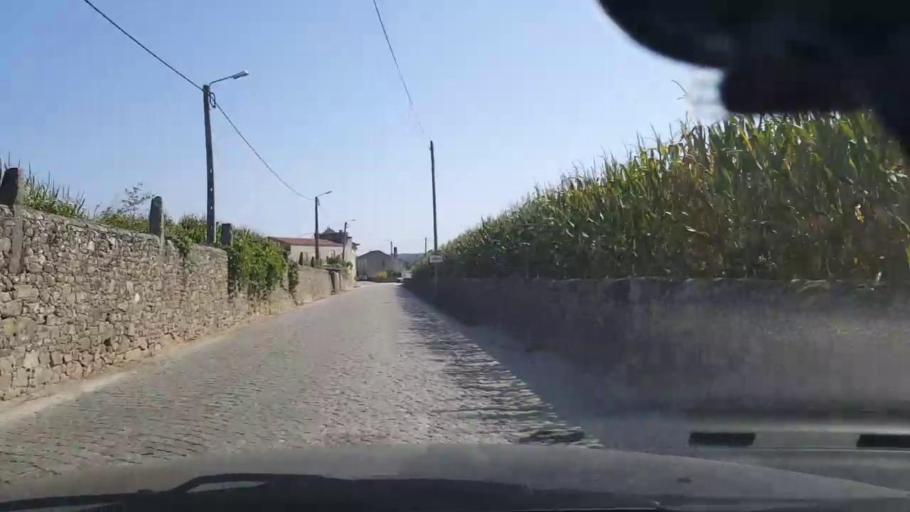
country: PT
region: Porto
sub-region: Povoa de Varzim
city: Pedroso
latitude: 41.4061
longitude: -8.6915
